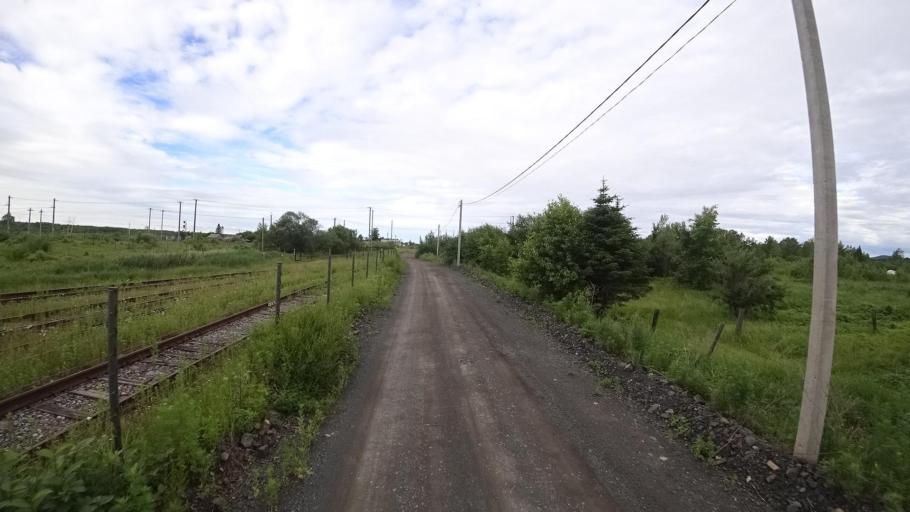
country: RU
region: Khabarovsk Krai
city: Amursk
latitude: 49.9057
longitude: 136.1452
